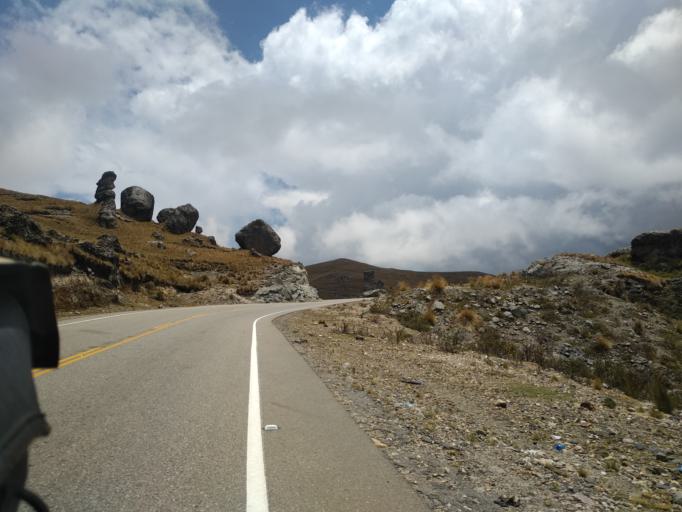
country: PE
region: La Libertad
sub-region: Provincia de Santiago de Chuco
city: Quiruvilca
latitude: -7.9736
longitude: -78.2210
